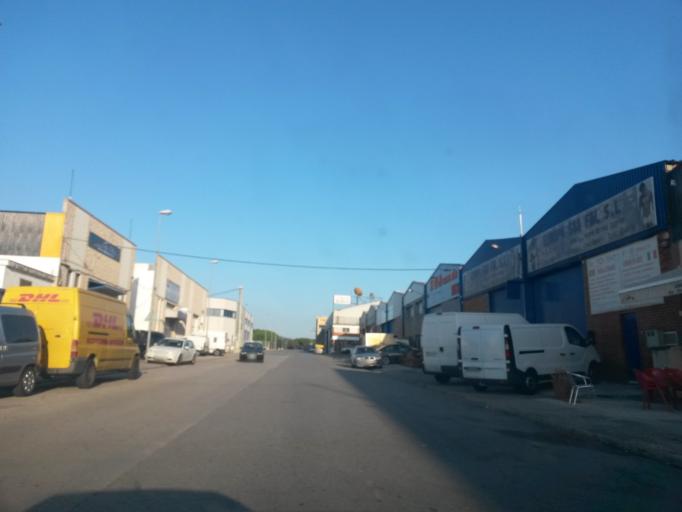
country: ES
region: Catalonia
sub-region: Provincia de Girona
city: Fornells de la Selva
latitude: 41.9352
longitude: 2.7989
